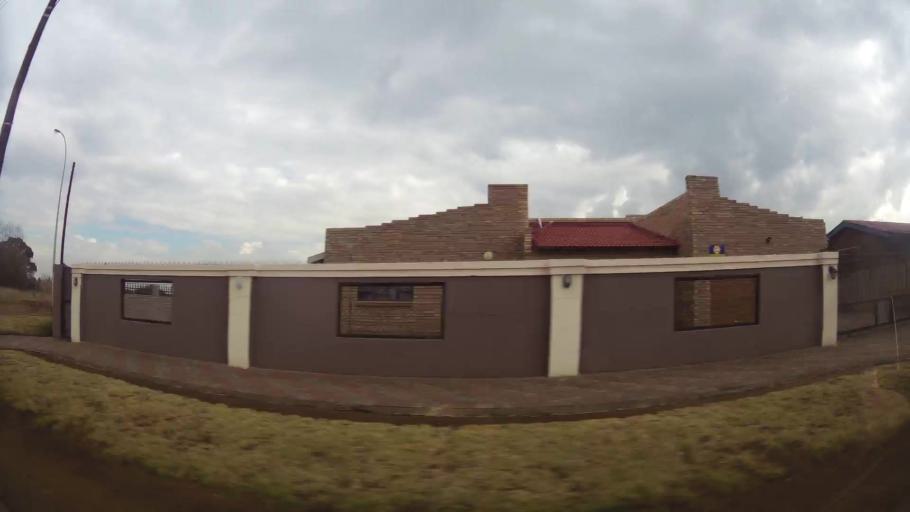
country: ZA
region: Gauteng
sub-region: Sedibeng District Municipality
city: Meyerton
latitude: -26.5804
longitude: 28.0028
